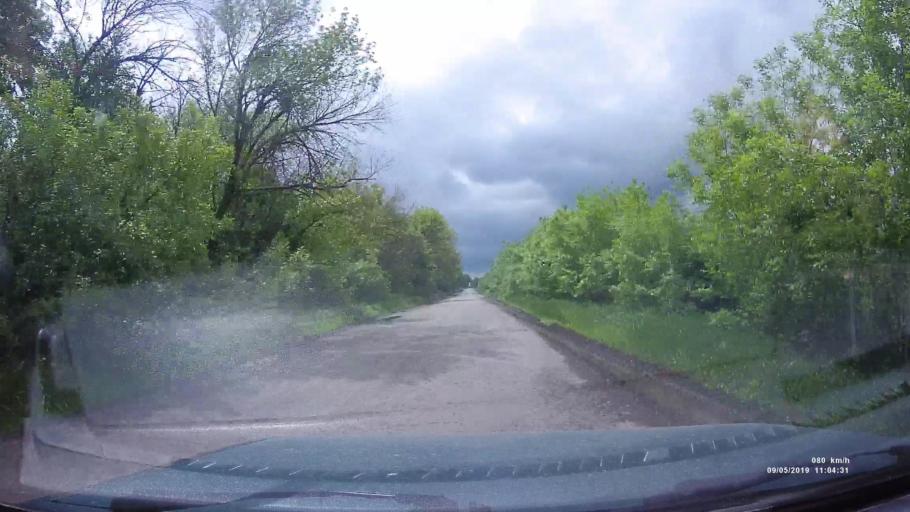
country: RU
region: Krasnodarskiy
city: Kanelovskaya
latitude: 46.8161
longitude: 39.2099
